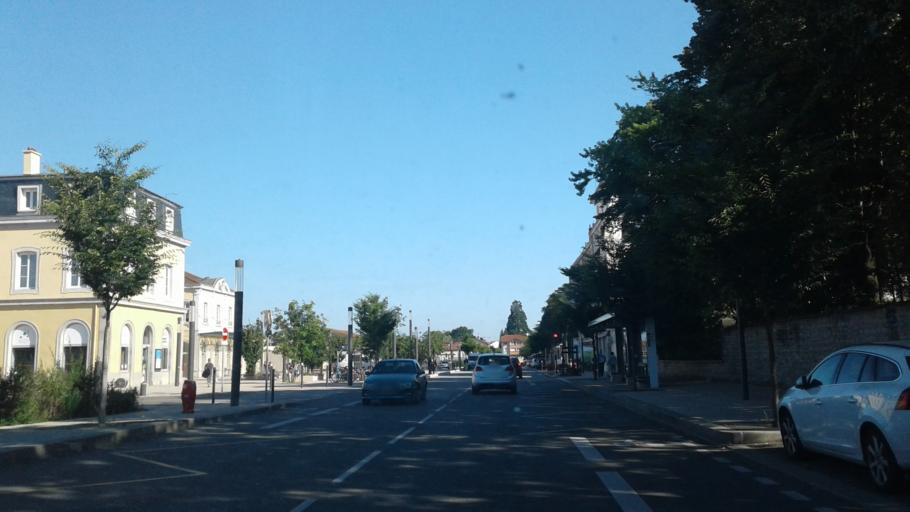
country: FR
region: Rhone-Alpes
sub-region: Departement de l'Ain
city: Peronnas
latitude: 46.1993
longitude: 5.2158
